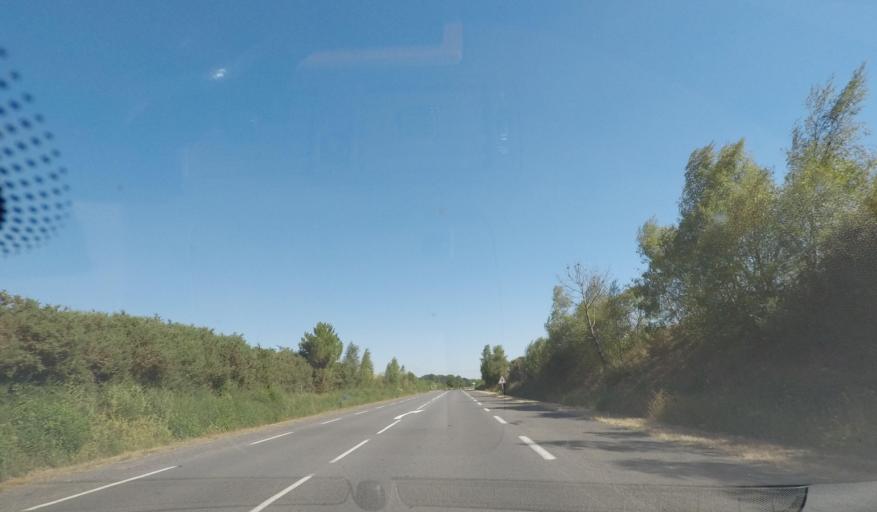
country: FR
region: Brittany
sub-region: Departement du Morbihan
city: Limerzel
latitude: 47.6137
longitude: -2.3947
